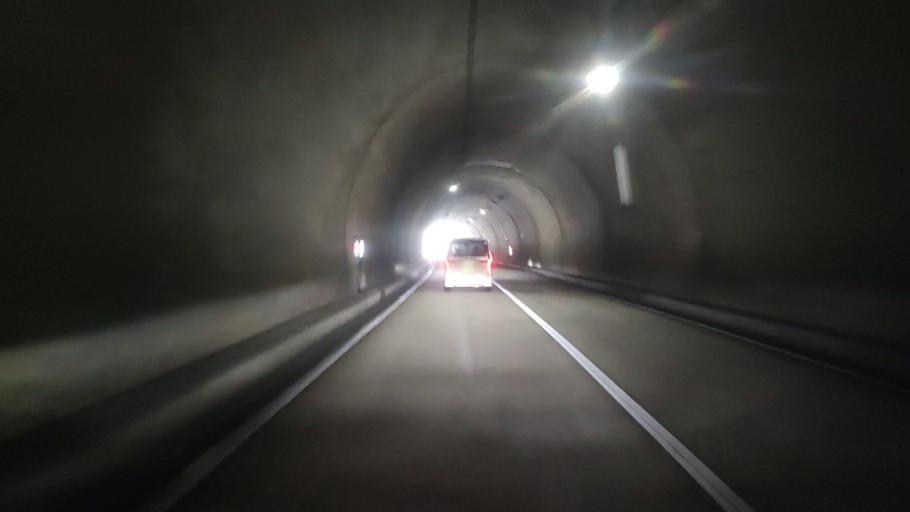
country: JP
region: Wakayama
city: Shingu
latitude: 33.8874
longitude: 135.8796
